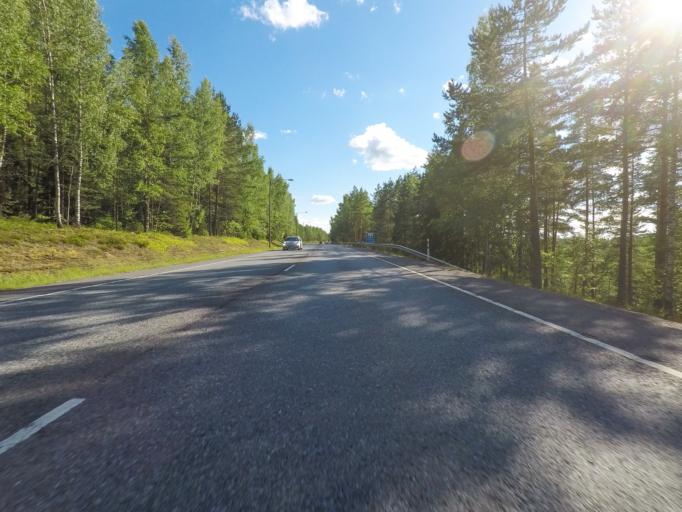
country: FI
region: Uusimaa
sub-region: Helsinki
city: Vihti
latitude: 60.3306
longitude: 24.2825
